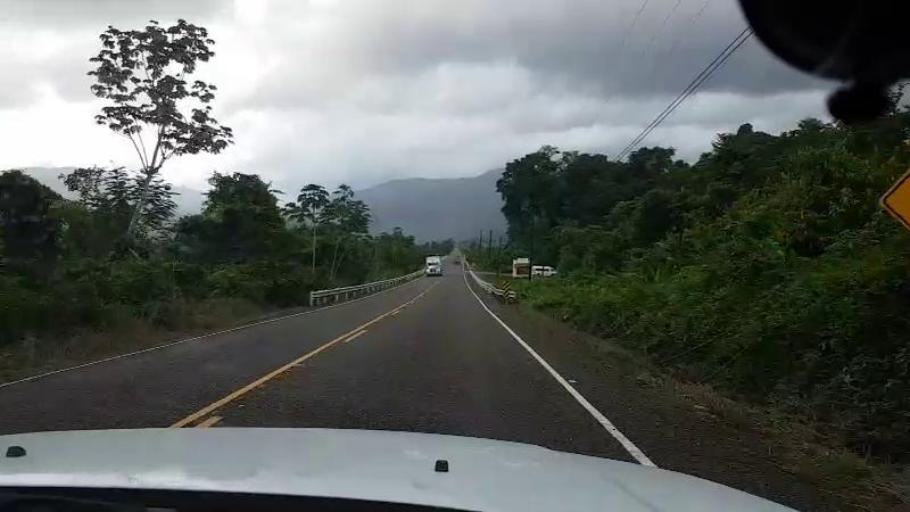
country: BZ
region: Cayo
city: Belmopan
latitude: 17.1120
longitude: -88.6584
